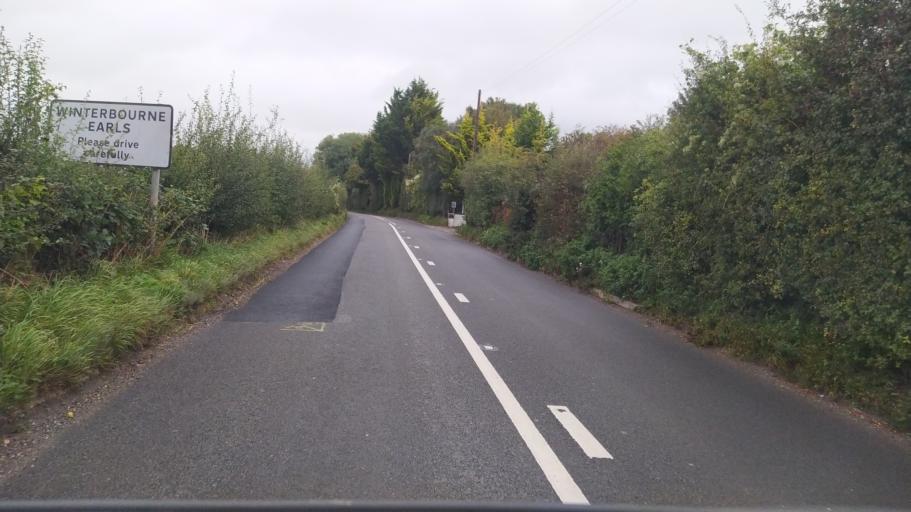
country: GB
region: England
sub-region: Wiltshire
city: Salisbury
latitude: 51.0984
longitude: -1.7584
